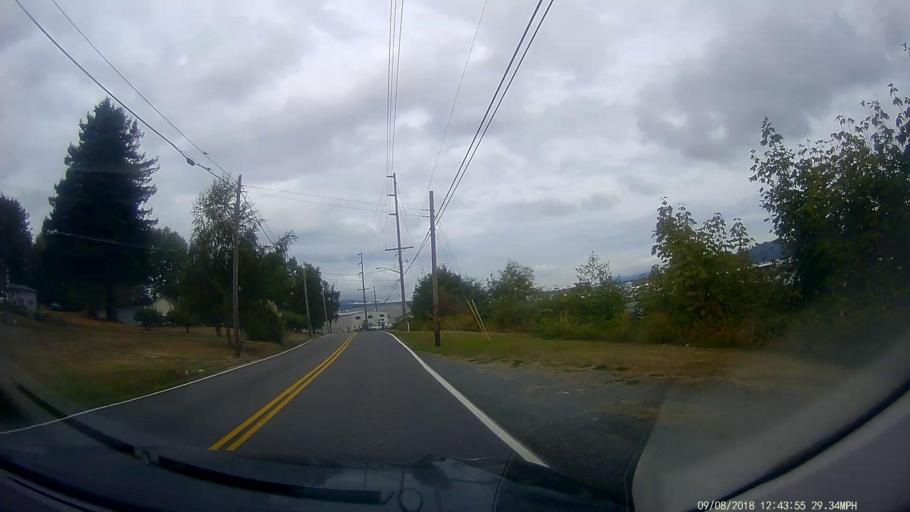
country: US
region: Washington
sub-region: Skagit County
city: Anacortes
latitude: 48.4929
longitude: -122.6011
